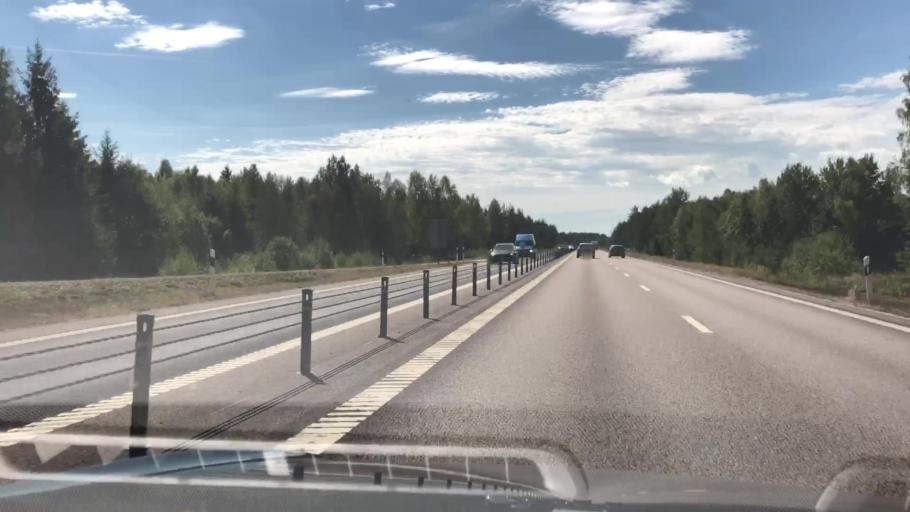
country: SE
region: Kalmar
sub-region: Torsas Kommun
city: Torsas
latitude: 56.5002
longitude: 16.0860
